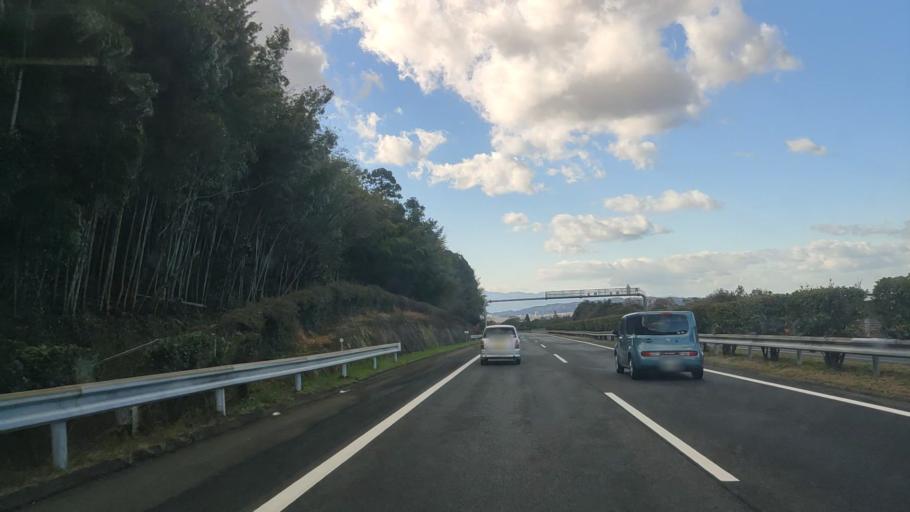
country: JP
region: Ehime
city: Niihama
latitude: 33.9290
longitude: 133.3404
